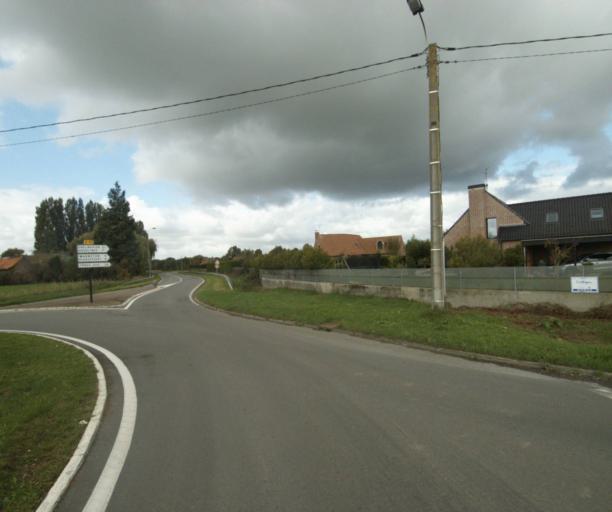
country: FR
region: Nord-Pas-de-Calais
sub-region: Departement du Nord
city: Verlinghem
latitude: 50.6973
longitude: 2.9770
